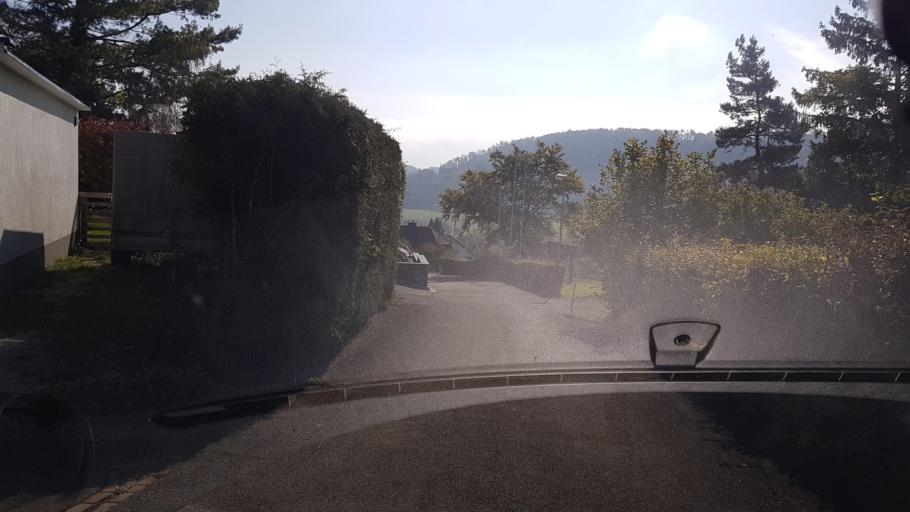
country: CH
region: Aargau
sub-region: Bezirk Laufenburg
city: Sulz
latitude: 47.5201
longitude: 8.1410
